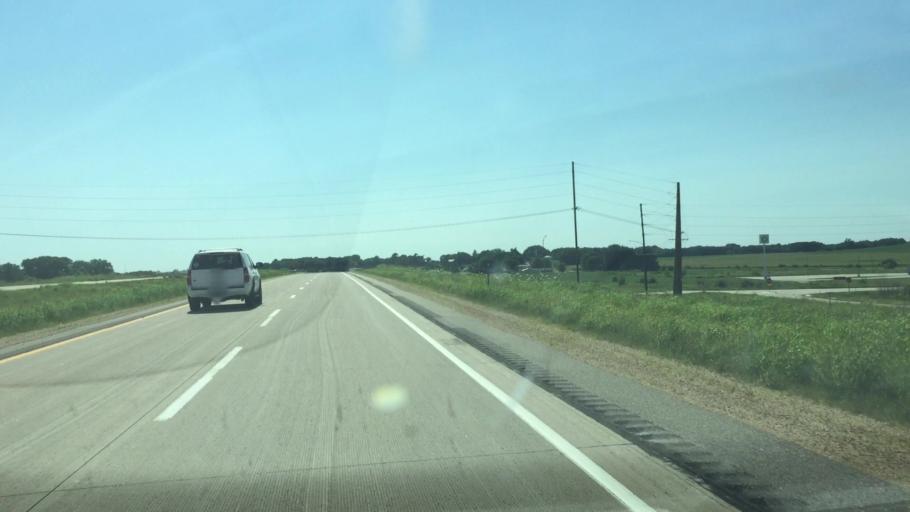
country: US
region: Iowa
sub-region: Jones County
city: Monticello
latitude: 42.2078
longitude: -91.1868
